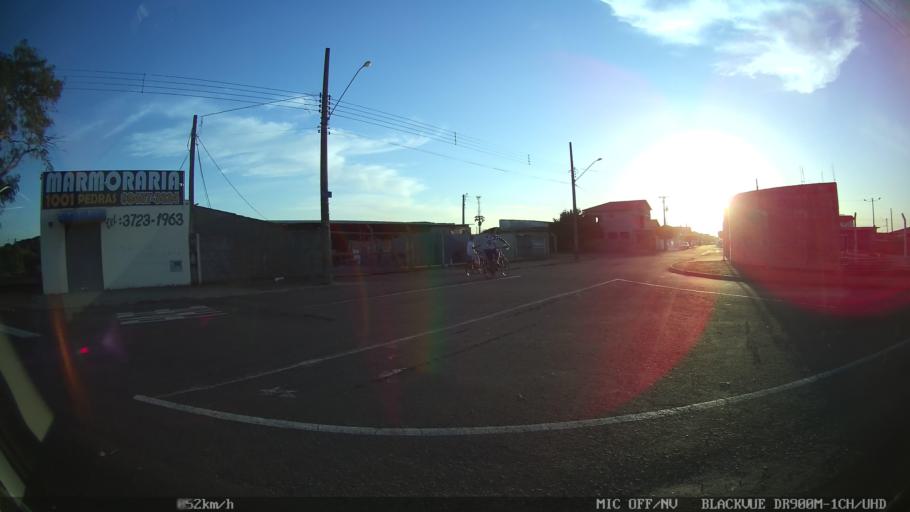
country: BR
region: Sao Paulo
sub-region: Franca
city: Franca
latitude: -20.4951
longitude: -47.4073
